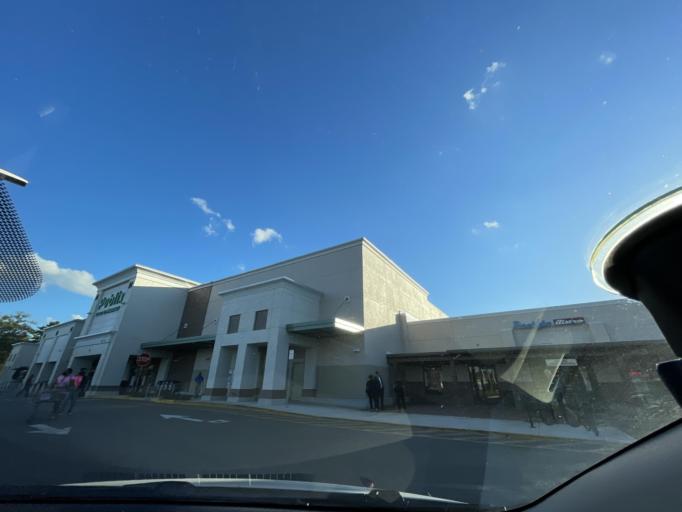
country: US
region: Florida
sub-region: Volusia County
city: Ormond Beach
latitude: 29.2832
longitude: -81.0839
